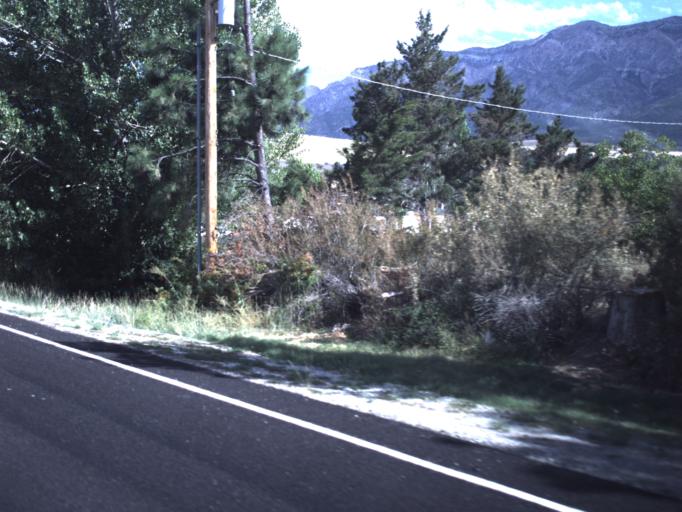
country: US
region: Utah
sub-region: Weber County
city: Pleasant View
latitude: 41.3137
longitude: -112.0110
